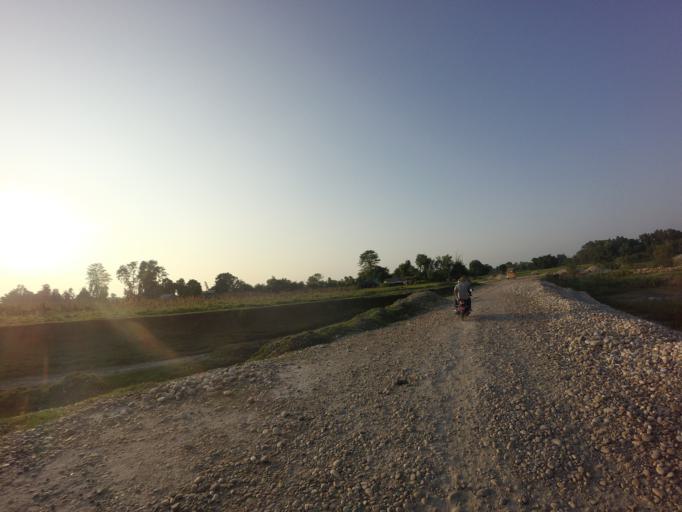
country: NP
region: Far Western
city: Tikapur
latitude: 28.4507
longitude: 81.0732
